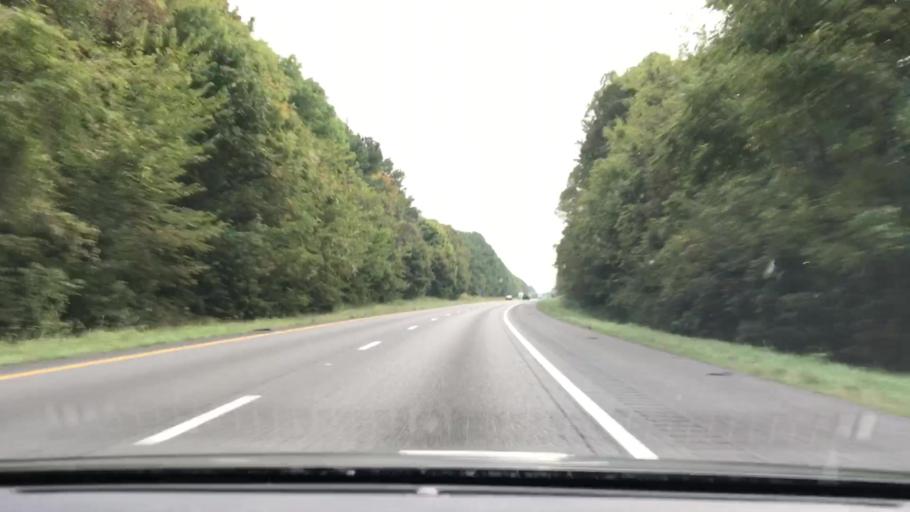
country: US
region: Tennessee
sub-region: Sumner County
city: Portland
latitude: 36.5851
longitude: -86.6082
